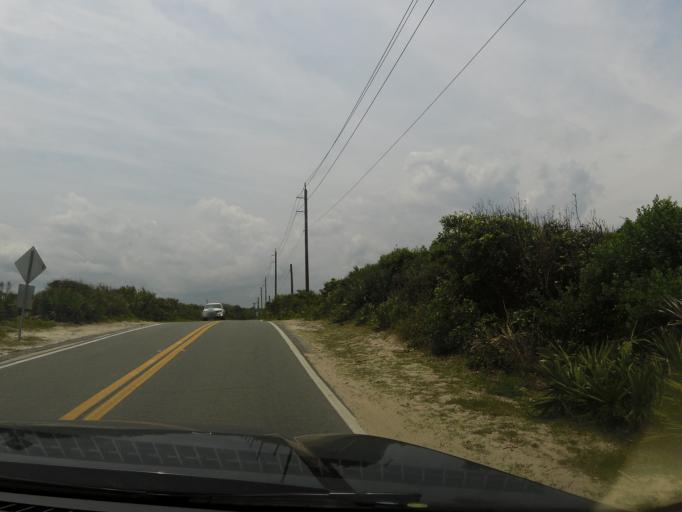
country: US
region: Florida
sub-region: Volusia County
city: Ormond-by-the-Sea
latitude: 29.4099
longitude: -81.0955
